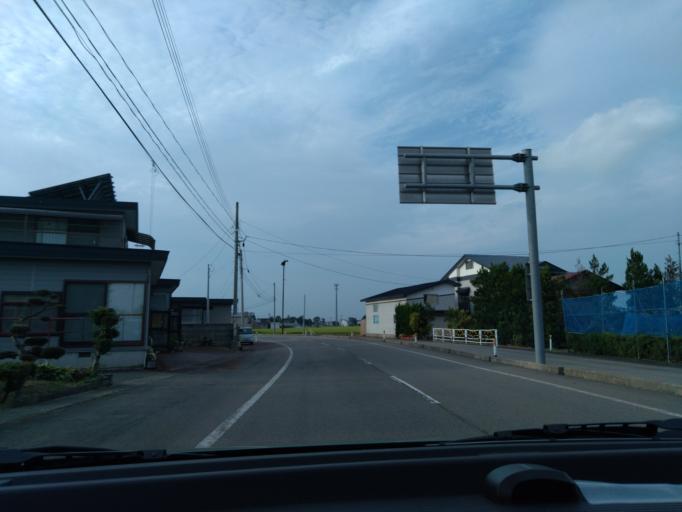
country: JP
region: Akita
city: Omagari
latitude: 39.3892
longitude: 140.5254
